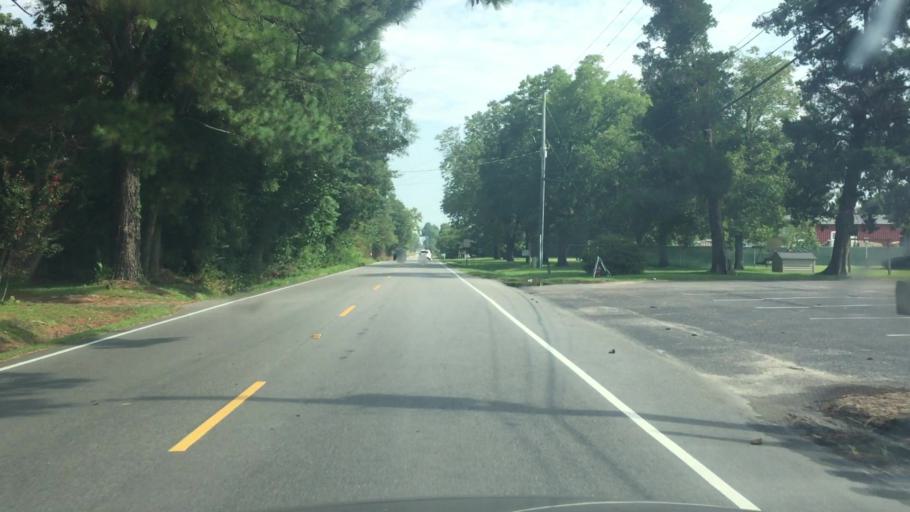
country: US
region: North Carolina
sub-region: Columbus County
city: Chadbourn
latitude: 34.3102
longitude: -78.8264
